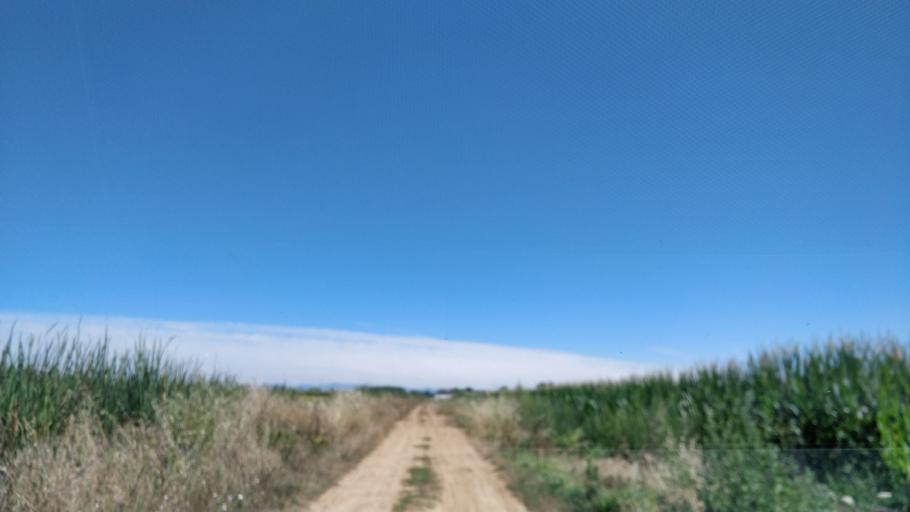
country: ES
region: Castille and Leon
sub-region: Provincia de Leon
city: Bustillo del Paramo
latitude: 42.4678
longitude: -5.8141
